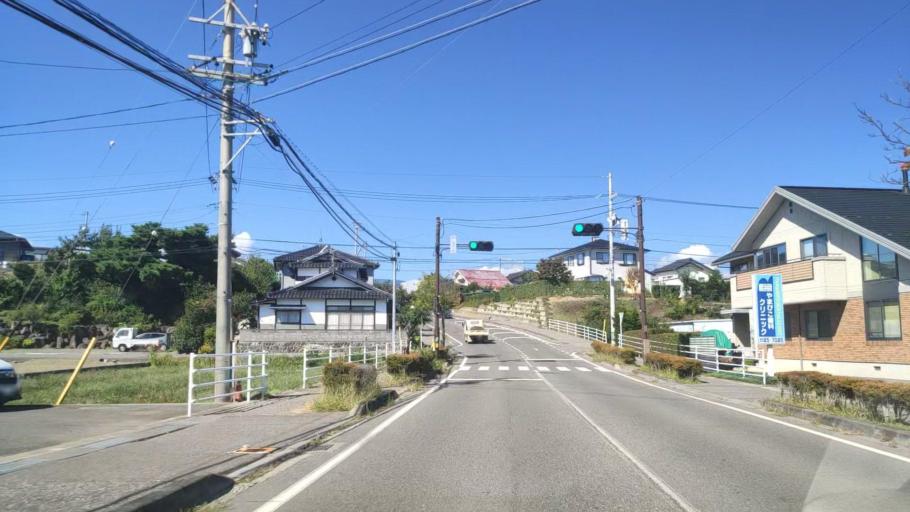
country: JP
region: Nagano
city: Shiojiri
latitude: 36.1654
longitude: 137.9339
